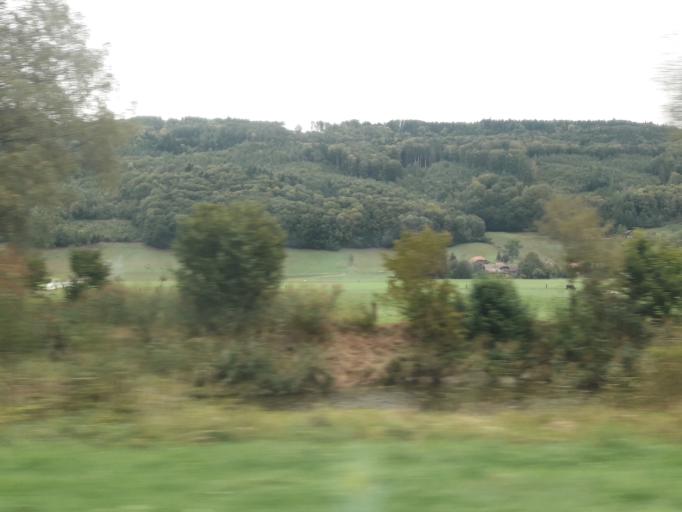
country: CH
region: Bern
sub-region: Bern-Mittelland District
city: Toffen
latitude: 46.8680
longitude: 7.4966
